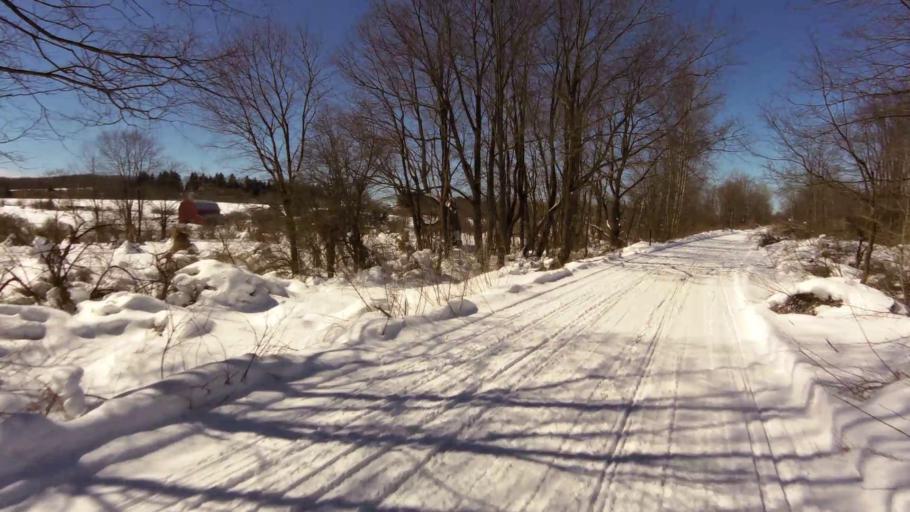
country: US
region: New York
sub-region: Cattaraugus County
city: Franklinville
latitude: 42.4230
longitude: -78.3748
